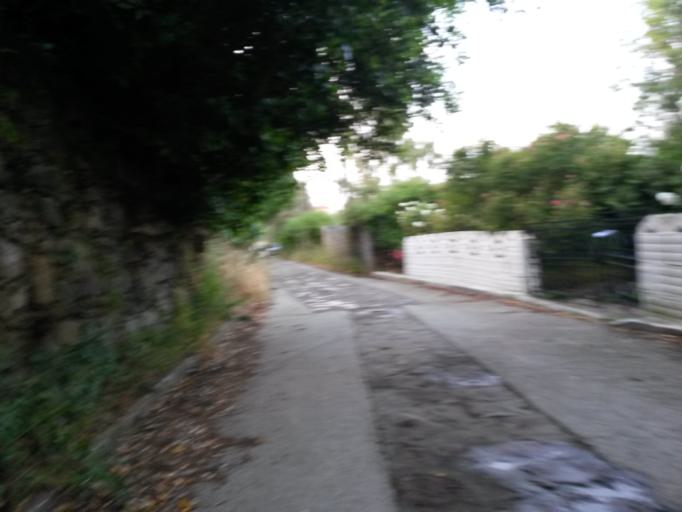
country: GR
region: North Aegean
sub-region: Nomos Lesvou
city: Pamfylla
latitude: 39.1731
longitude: 26.4991
